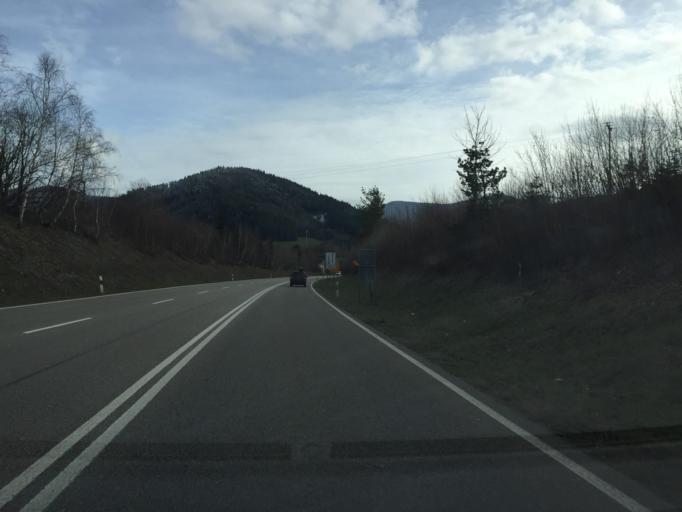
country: DE
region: Baden-Wuerttemberg
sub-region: Freiburg Region
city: Stegen
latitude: 47.9651
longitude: 7.9866
